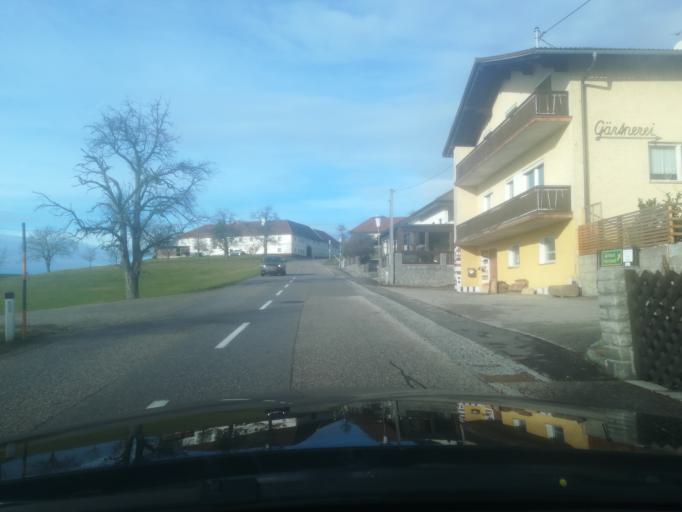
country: AT
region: Upper Austria
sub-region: Politischer Bezirk Perg
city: Perg
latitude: 48.3362
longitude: 14.6240
